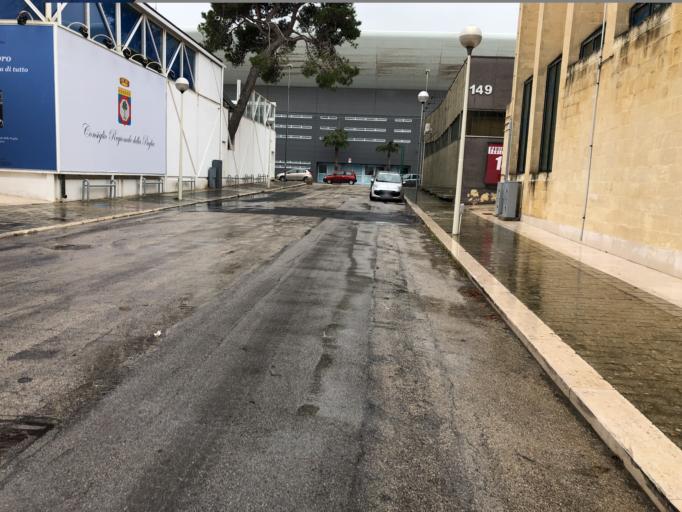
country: IT
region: Apulia
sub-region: Provincia di Bari
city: Bari
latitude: 41.1361
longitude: 16.8382
